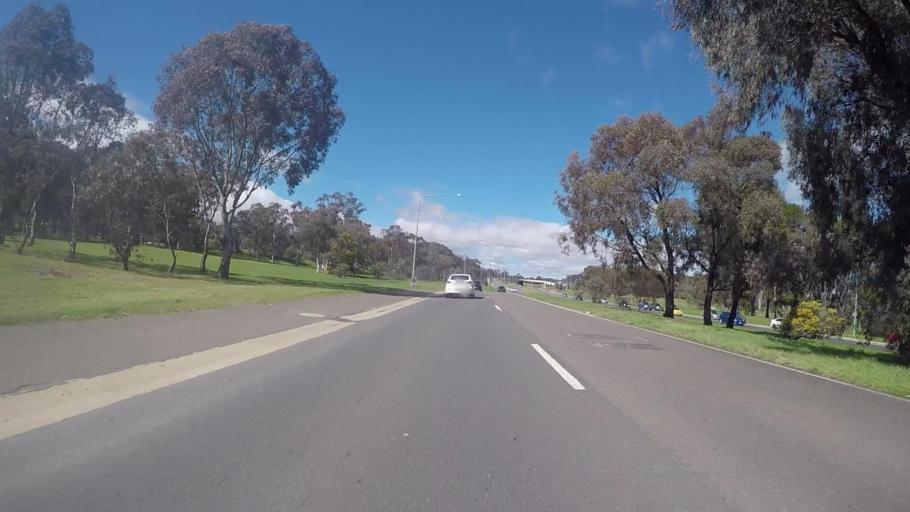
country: AU
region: Australian Capital Territory
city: Canberra
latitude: -35.2948
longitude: 149.1453
